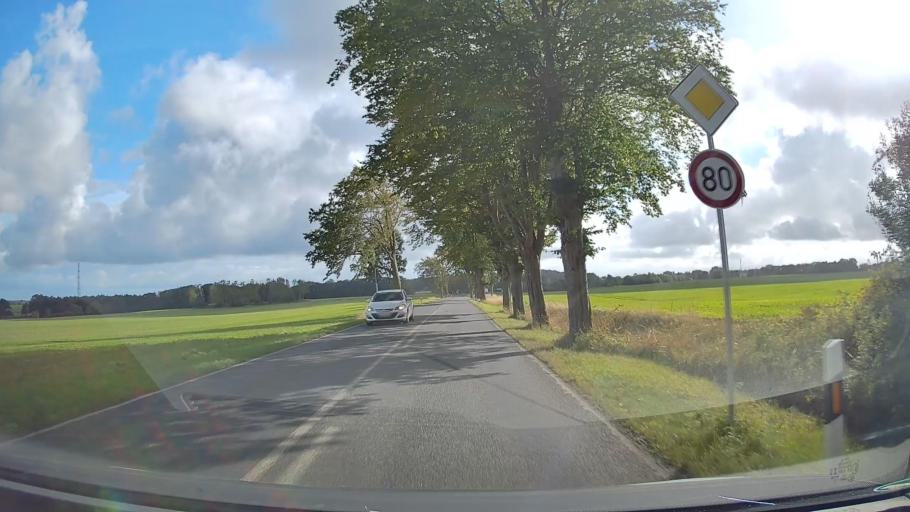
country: DE
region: Mecklenburg-Vorpommern
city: Putbus
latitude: 54.3685
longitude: 13.4789
